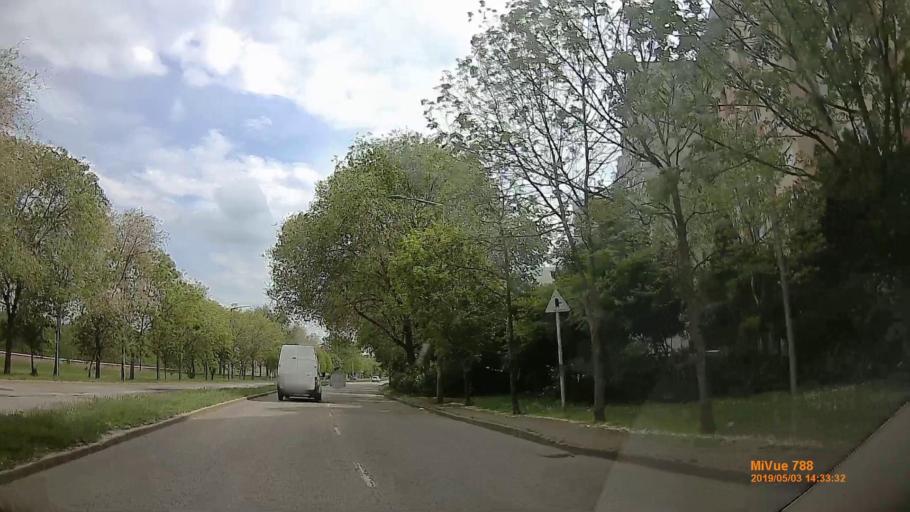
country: HU
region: Jasz-Nagykun-Szolnok
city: Szolnok
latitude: 47.1797
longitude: 20.2005
